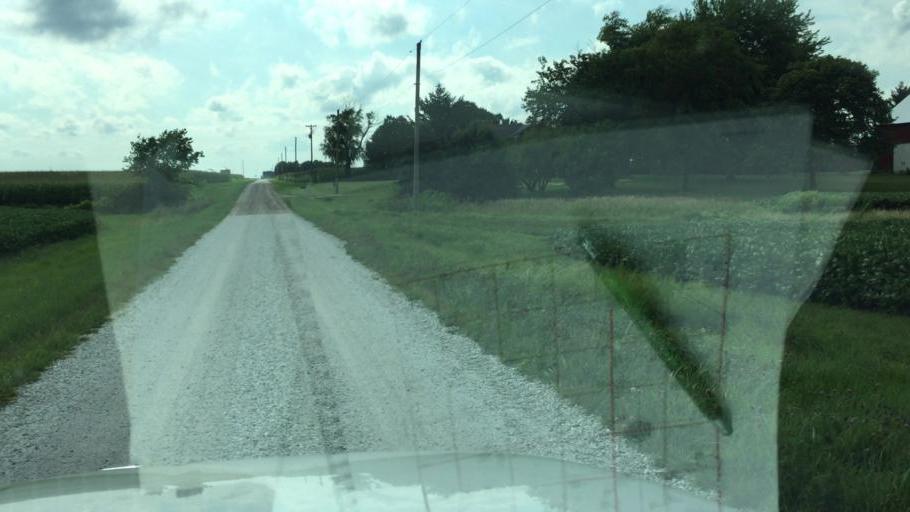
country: US
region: Illinois
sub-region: Hancock County
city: Carthage
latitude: 40.5356
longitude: -91.1713
